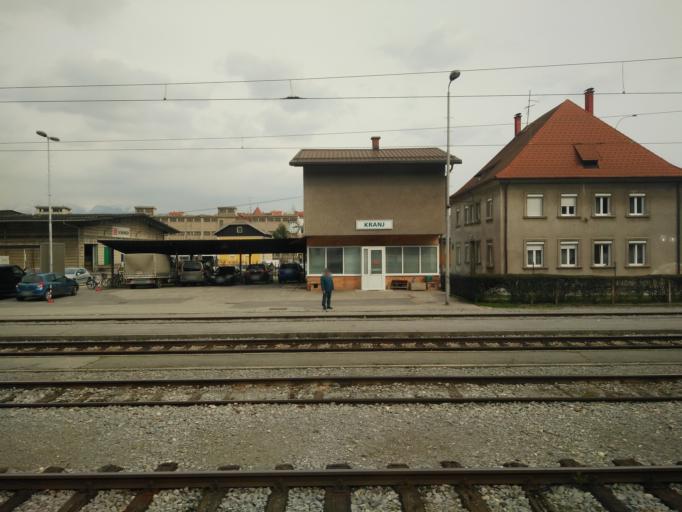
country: SI
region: Kranj
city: Kranj
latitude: 46.2383
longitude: 14.3482
